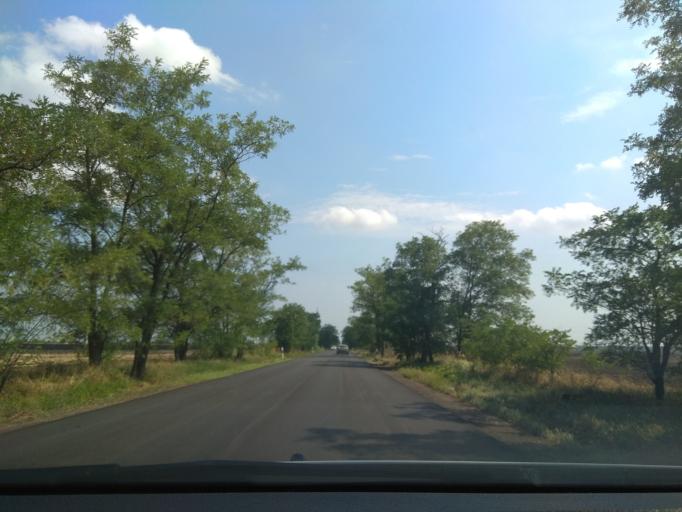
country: HU
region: Heves
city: Szihalom
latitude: 47.8167
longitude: 20.5145
